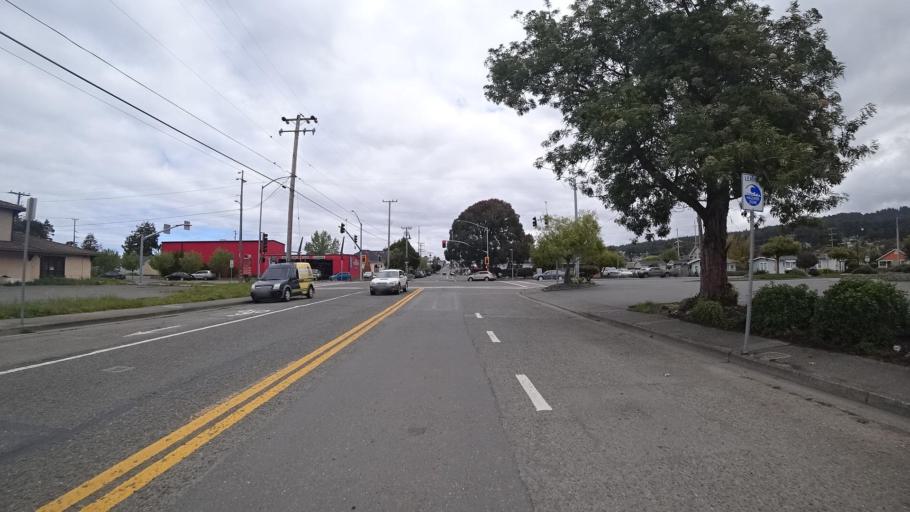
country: US
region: California
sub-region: Humboldt County
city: Arcata
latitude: 40.8645
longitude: -124.0874
